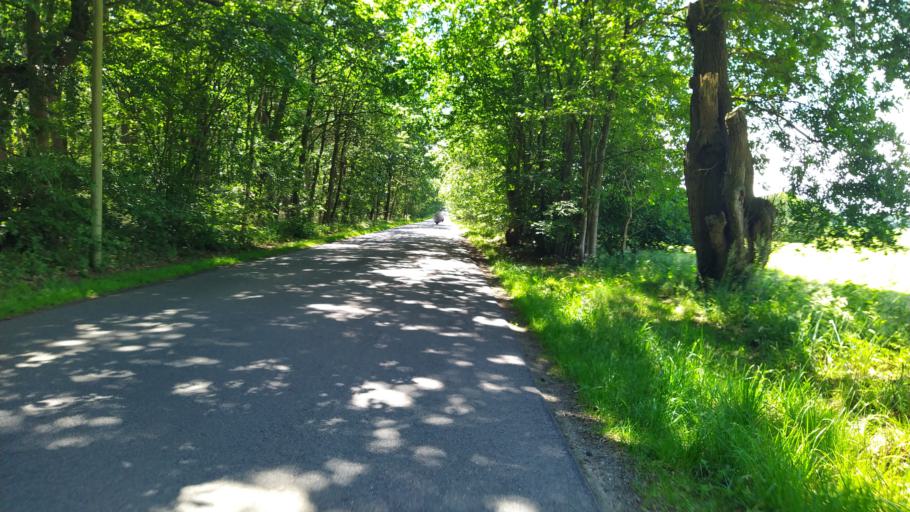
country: DE
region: Lower Saxony
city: Oldendorf
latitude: 53.5624
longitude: 9.2403
